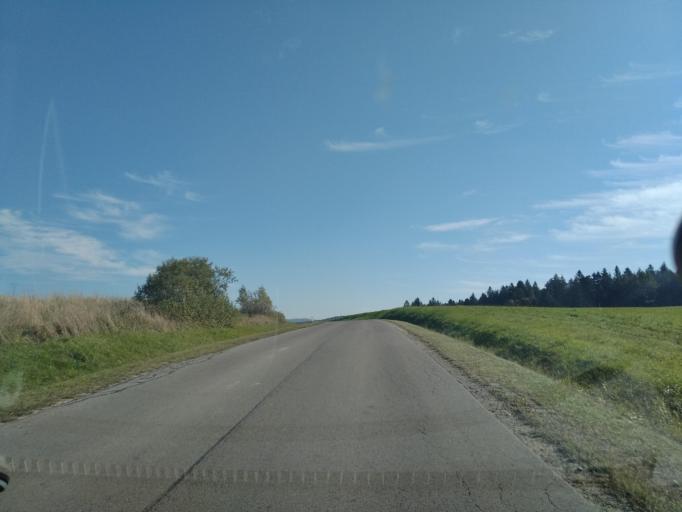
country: PL
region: Subcarpathian Voivodeship
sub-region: Powiat krosnienski
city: Jasliska
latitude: 49.4142
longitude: 21.9288
